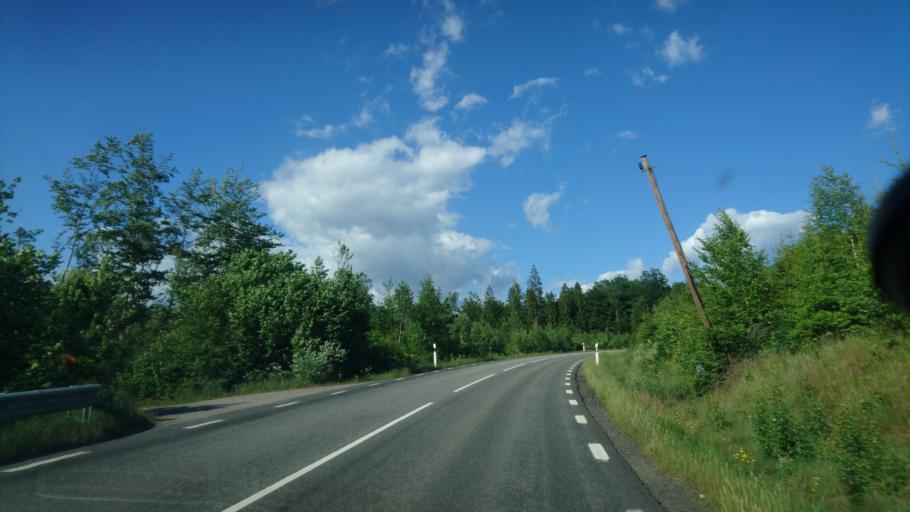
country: SE
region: Skane
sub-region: Osby Kommun
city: Lonsboda
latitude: 56.3917
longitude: 14.3759
